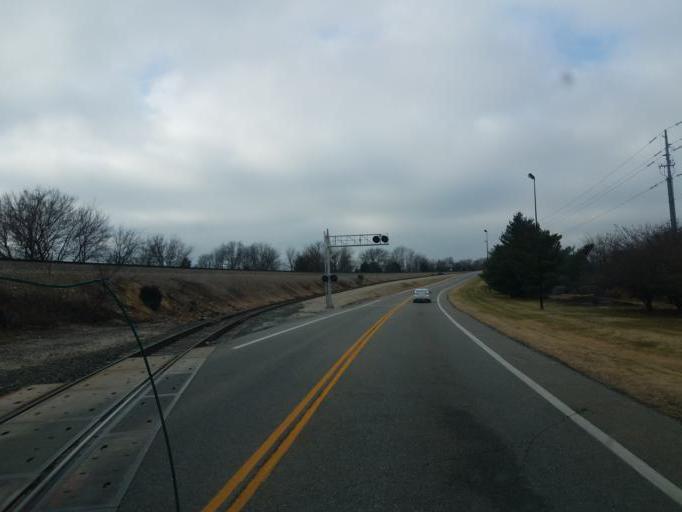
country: US
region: Missouri
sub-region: Greene County
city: Strafford
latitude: 37.2396
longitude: -93.1993
